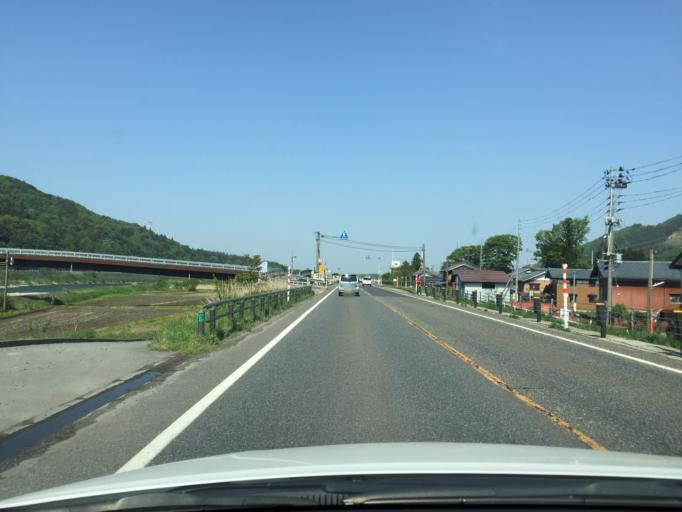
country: JP
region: Niigata
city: Gosen
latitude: 37.7384
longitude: 139.2841
